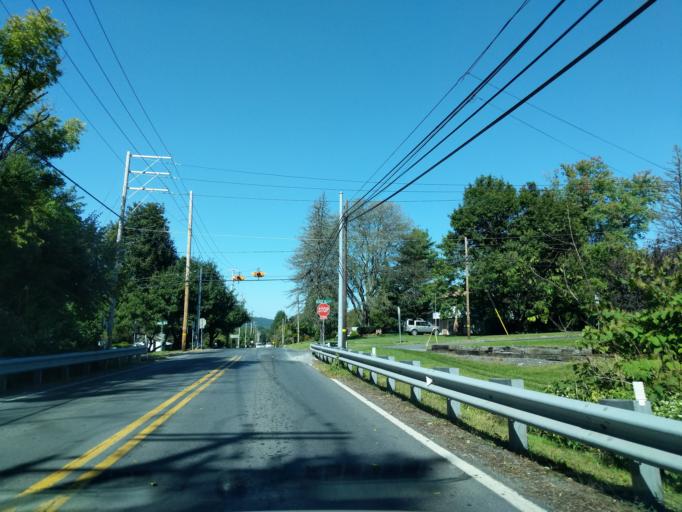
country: US
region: Pennsylvania
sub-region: Lehigh County
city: Coopersburg
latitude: 40.4976
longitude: -75.4424
